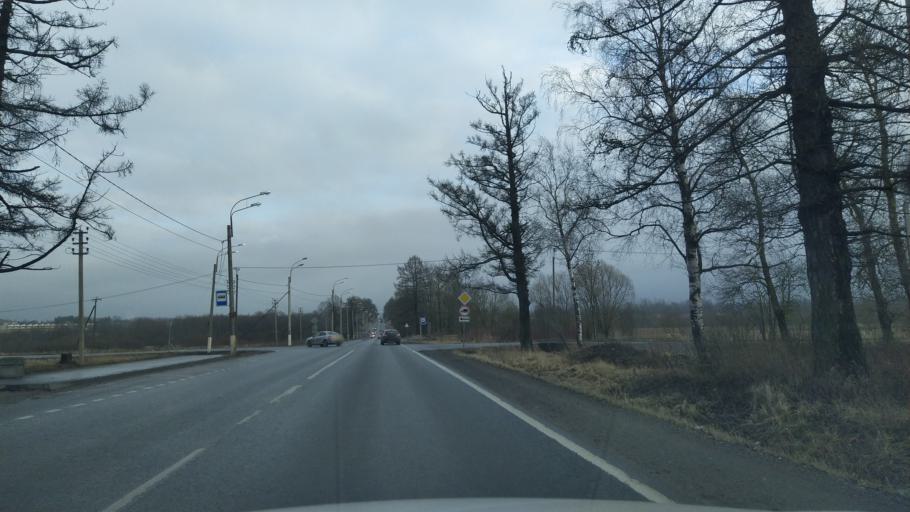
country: RU
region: St.-Petersburg
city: Aleksandrovskaya
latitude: 59.7094
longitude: 30.3233
